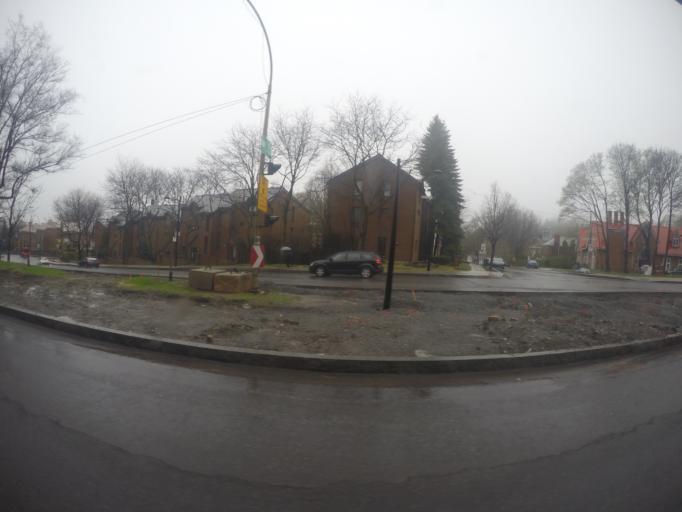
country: CA
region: Quebec
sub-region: Montreal
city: Montreal
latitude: 45.5001
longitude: -73.5714
